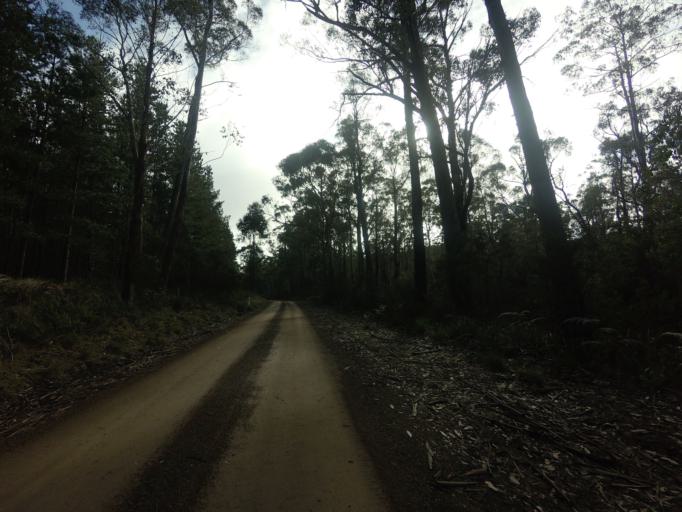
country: AU
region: Tasmania
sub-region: Derwent Valley
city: New Norfolk
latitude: -42.7658
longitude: 146.8988
